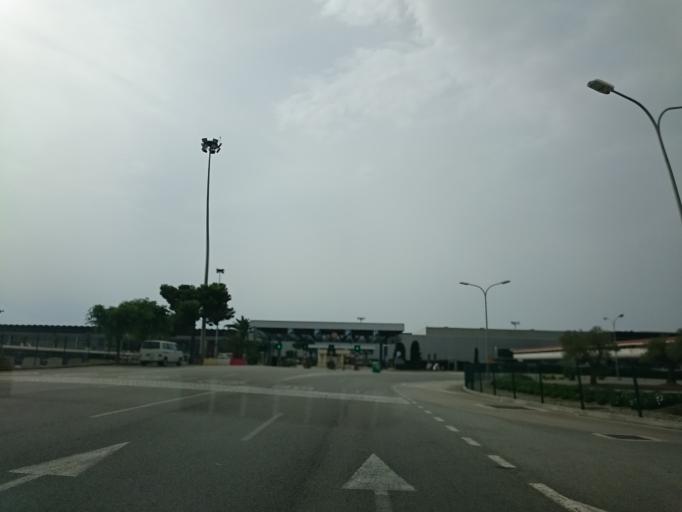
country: ES
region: Catalonia
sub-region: Provincia de Barcelona
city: El Prat de Llobregat
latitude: 41.3047
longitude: 2.0748
